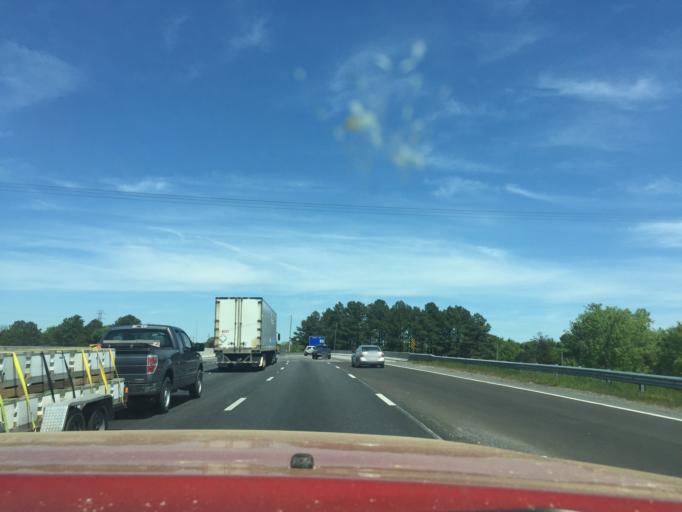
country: US
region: North Carolina
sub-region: Mecklenburg County
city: Pineville
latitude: 35.0909
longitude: -80.9338
